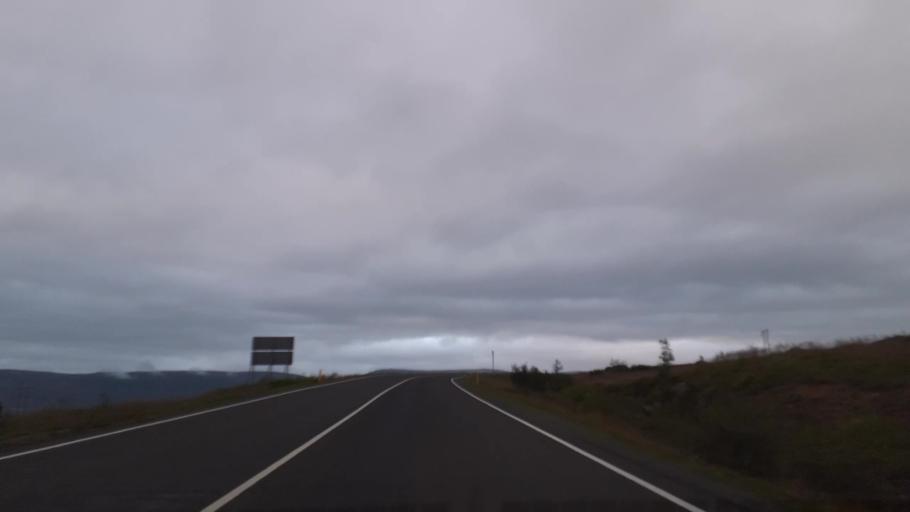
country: IS
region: Northeast
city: Akureyri
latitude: 65.7478
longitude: -18.2186
